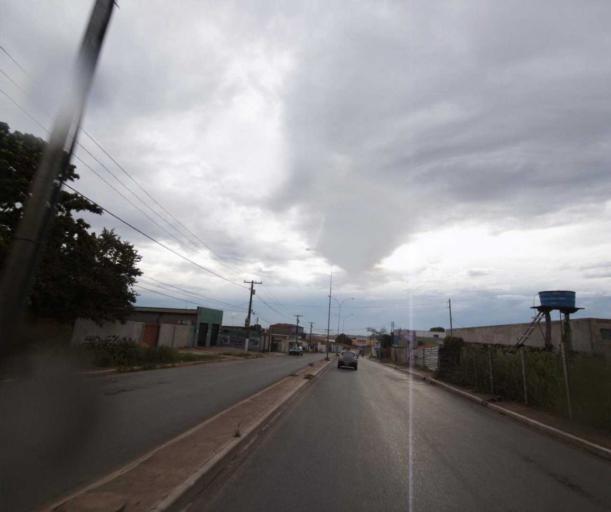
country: BR
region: Mato Grosso
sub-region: Varzea Grande
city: Varzea Grande
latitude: -15.6485
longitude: -56.1439
